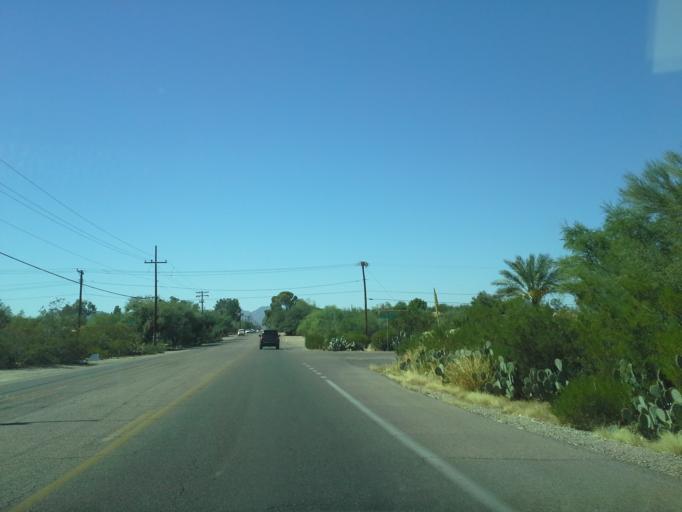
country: US
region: Arizona
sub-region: Pima County
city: Catalina Foothills
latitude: 32.2723
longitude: -110.9363
